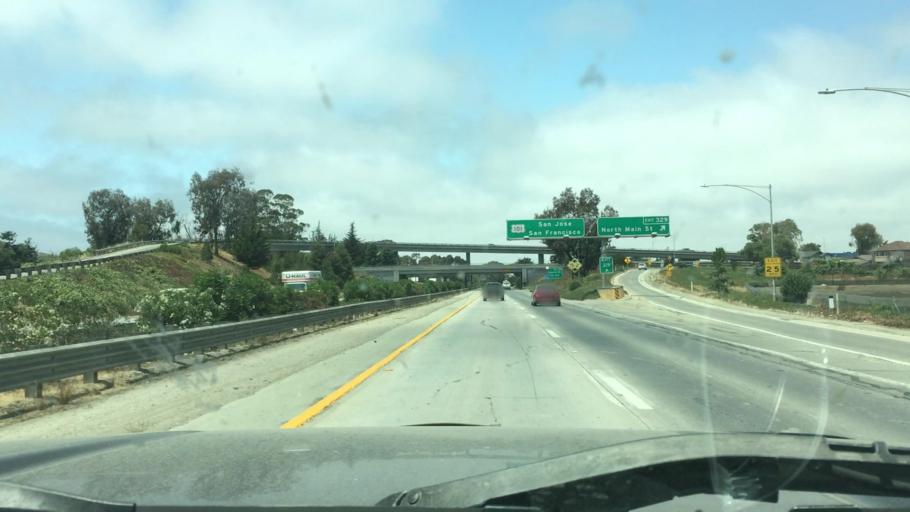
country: US
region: California
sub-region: Monterey County
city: Salinas
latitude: 36.6859
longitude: -121.6503
